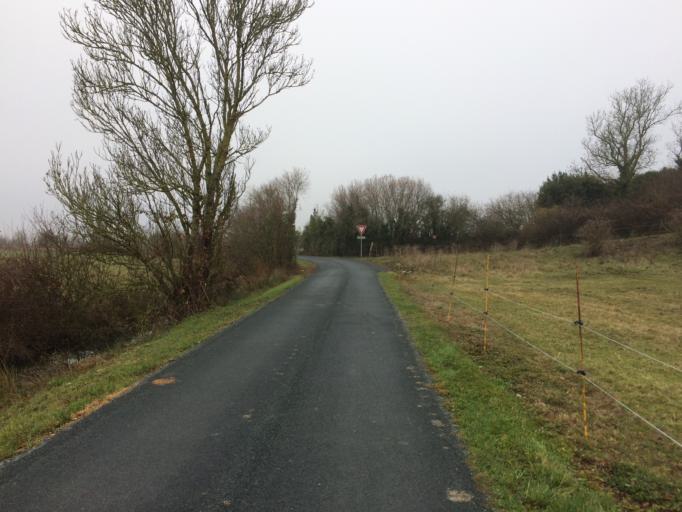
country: FR
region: Pays de la Loire
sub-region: Departement de la Vendee
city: Chaille-les-Marais
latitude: 46.3815
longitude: -1.0259
